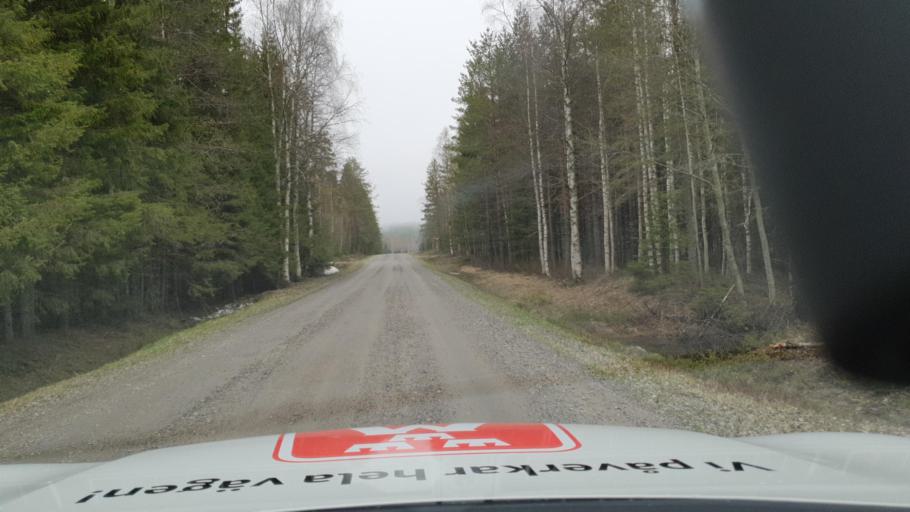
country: SE
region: Vaesterbotten
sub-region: Nordmalings Kommun
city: Nordmaling
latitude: 63.7326
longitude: 19.5027
